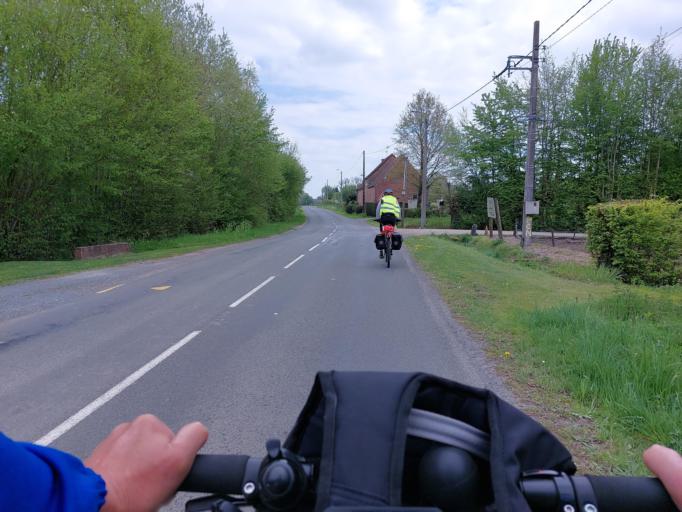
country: FR
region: Nord-Pas-de-Calais
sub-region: Departement du Nord
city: La Longueville
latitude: 50.2761
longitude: 3.8792
